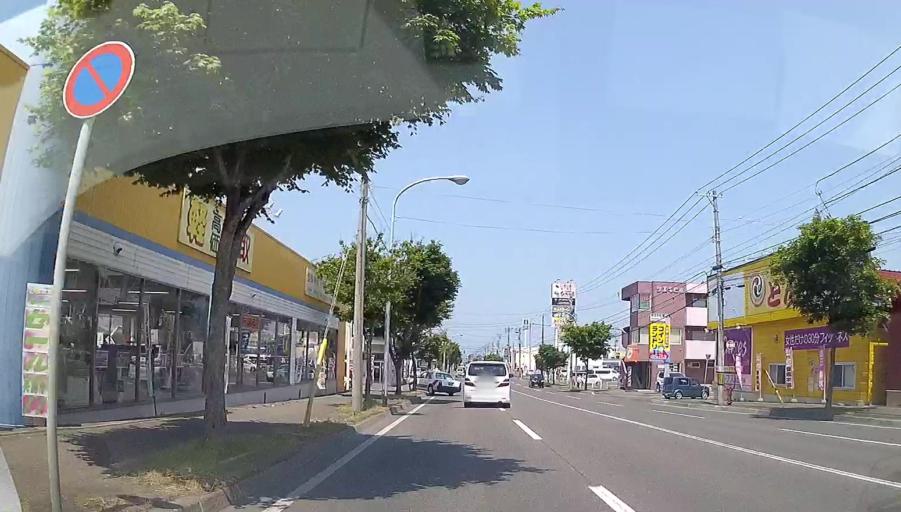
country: JP
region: Hokkaido
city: Obihiro
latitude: 42.8954
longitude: 143.2008
